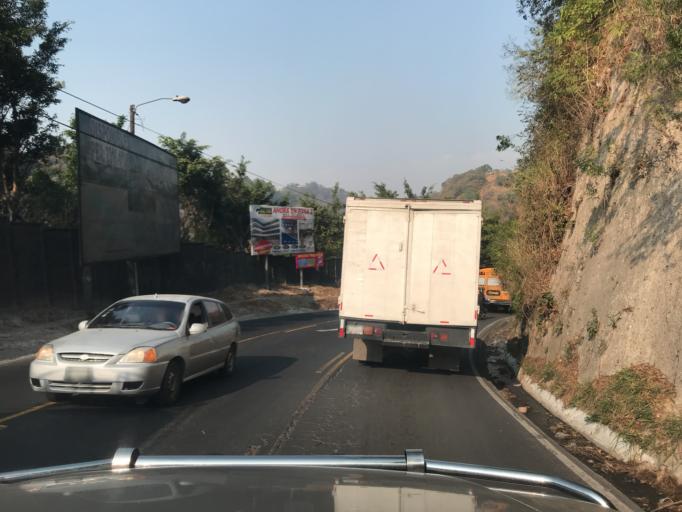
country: GT
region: Guatemala
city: Santa Catarina Pinula
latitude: 14.5559
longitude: -90.5274
